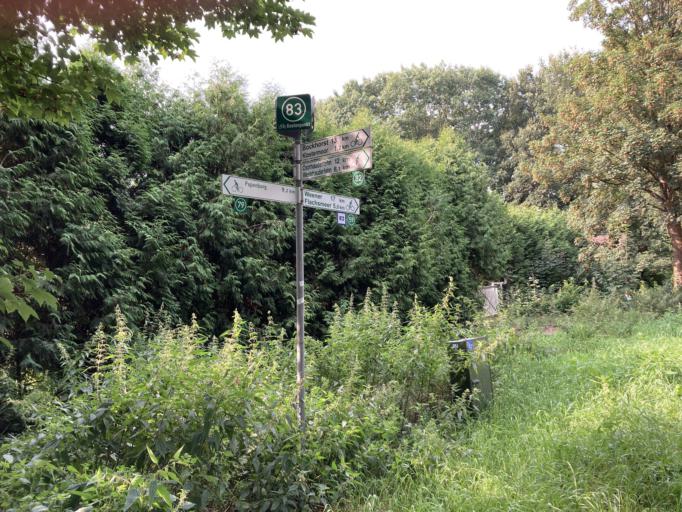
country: DE
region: Lower Saxony
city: Bockhorst
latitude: 53.0896
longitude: 7.5077
